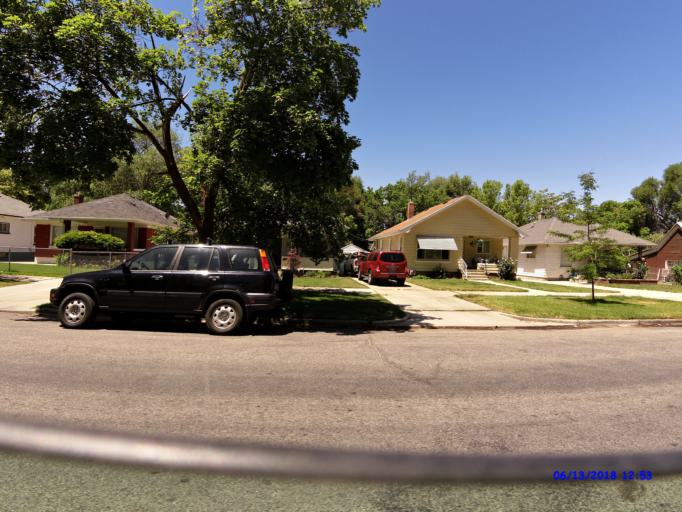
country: US
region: Utah
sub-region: Weber County
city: Ogden
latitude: 41.2127
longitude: -111.9595
